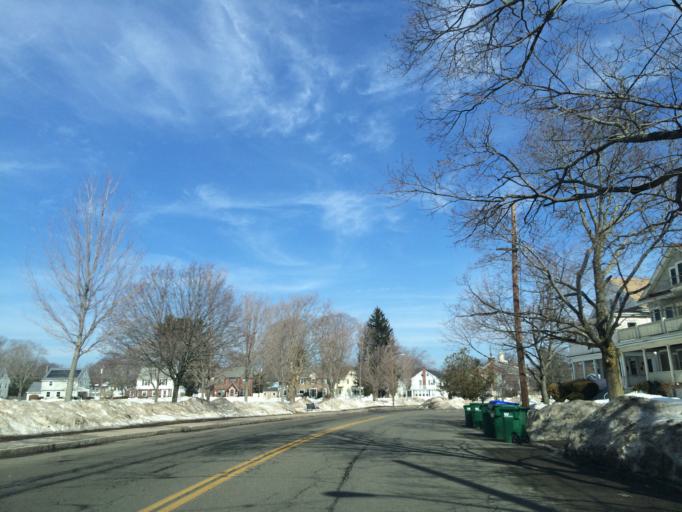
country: US
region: Massachusetts
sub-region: Middlesex County
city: Arlington
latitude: 42.4251
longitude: -71.1348
